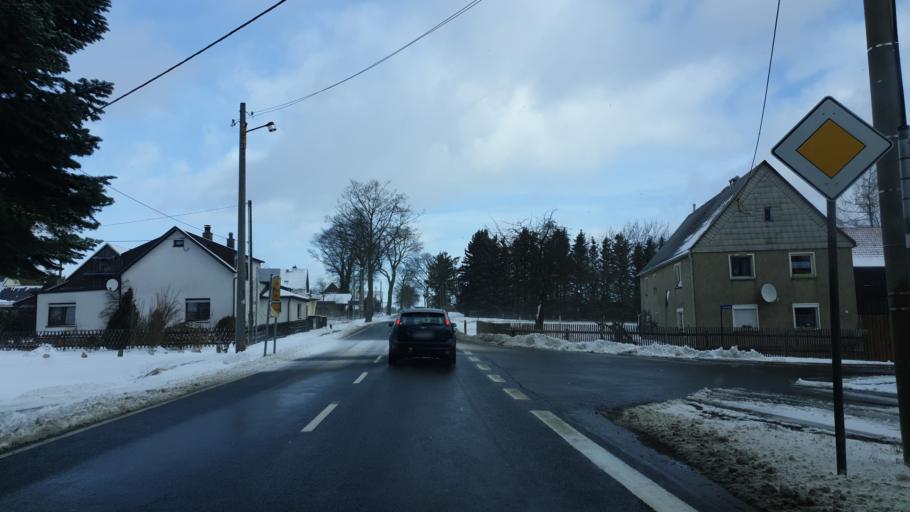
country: DE
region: Saxony
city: Eichigt
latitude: 50.3432
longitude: 12.1609
